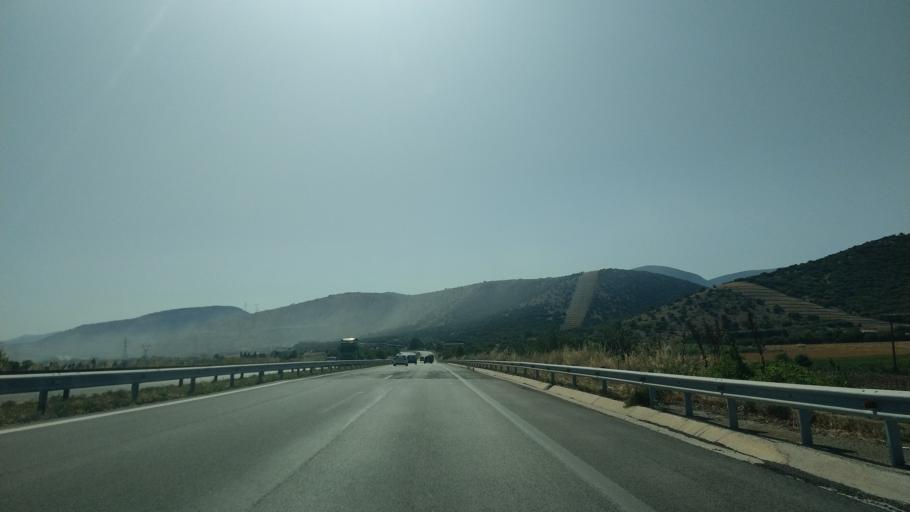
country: GR
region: East Macedonia and Thrace
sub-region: Nomos Kavalas
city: Nea Karvali
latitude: 40.9703
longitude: 24.5014
